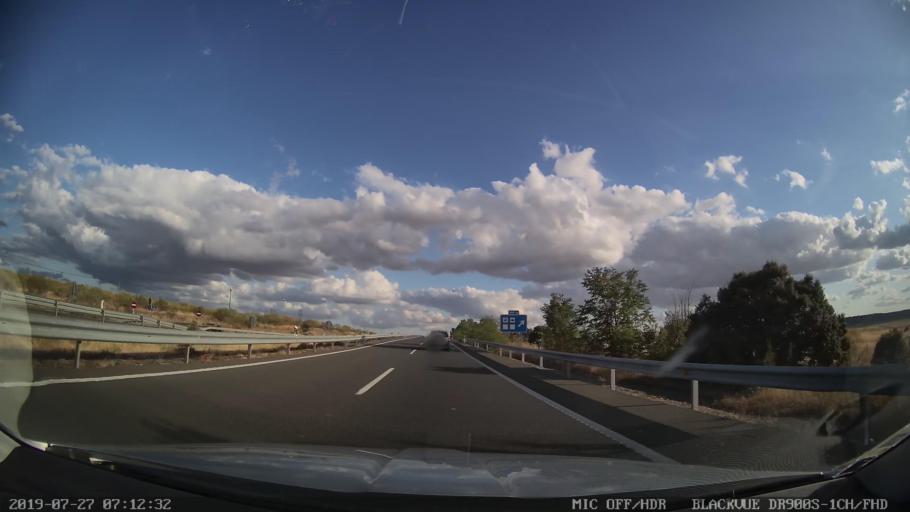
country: ES
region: Extremadura
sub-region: Provincia de Caceres
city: Trujillo
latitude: 39.5298
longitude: -5.8346
